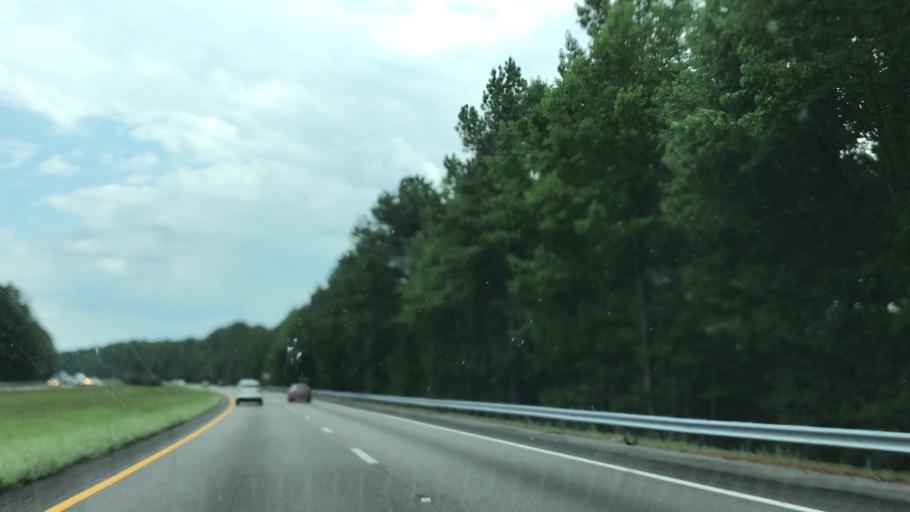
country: US
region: South Carolina
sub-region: Richland County
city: Blythewood
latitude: 34.2444
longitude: -80.9999
